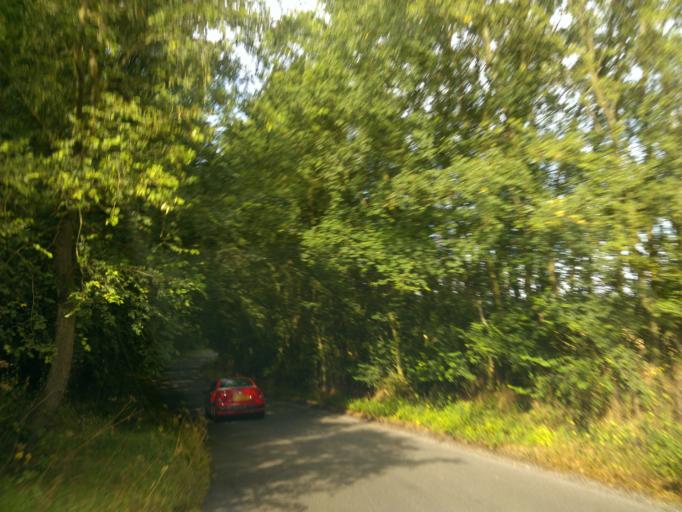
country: GB
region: England
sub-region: Essex
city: Sible Hedingham
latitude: 51.9808
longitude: 0.6135
